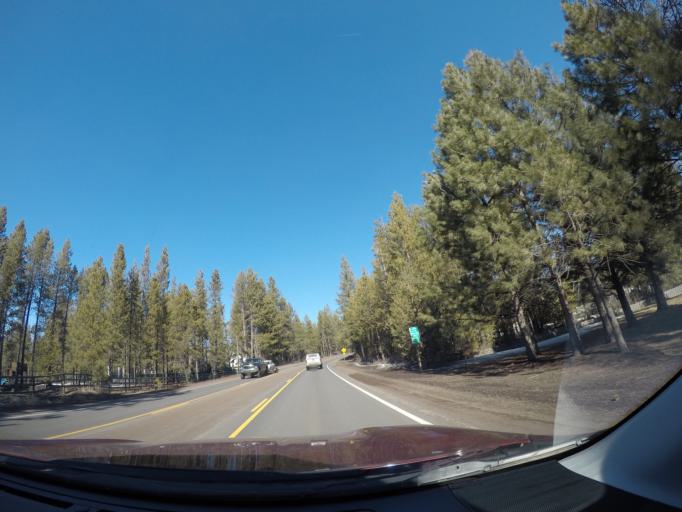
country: US
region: Oregon
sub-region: Deschutes County
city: Sunriver
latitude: 43.8673
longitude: -121.4364
